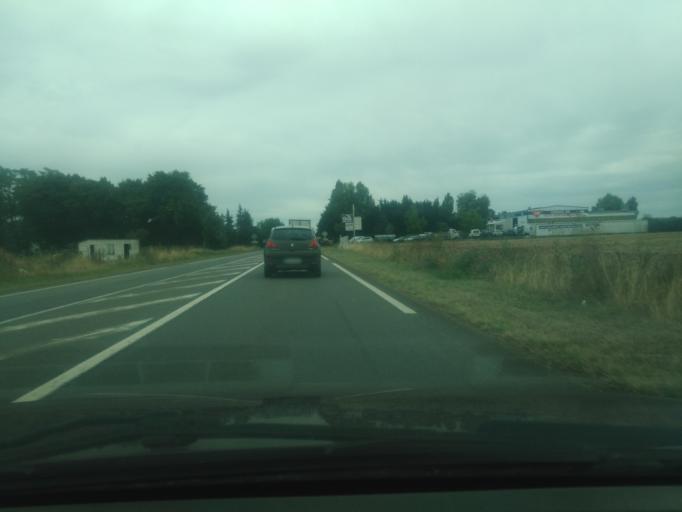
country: FR
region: Poitou-Charentes
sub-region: Departement de la Vienne
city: Saint-Savin
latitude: 46.5636
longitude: 0.8556
